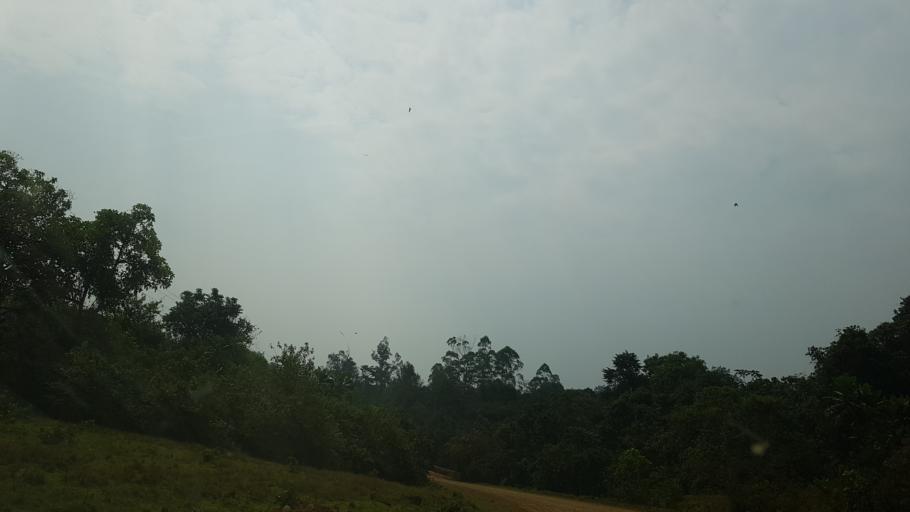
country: ET
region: Oromiya
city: Gore
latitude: 7.8744
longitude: 35.4783
